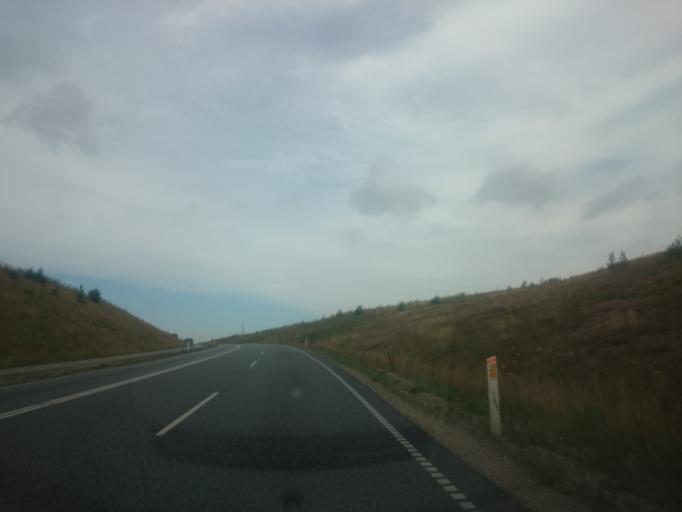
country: DK
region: South Denmark
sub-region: Vejle Kommune
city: Jelling
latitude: 55.6898
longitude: 9.3800
